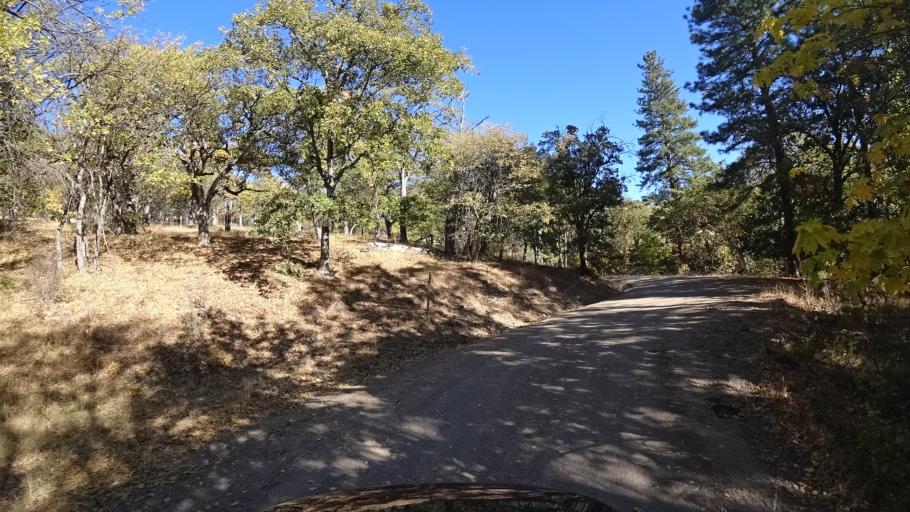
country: US
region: California
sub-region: Siskiyou County
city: Montague
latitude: 41.9913
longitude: -122.3164
